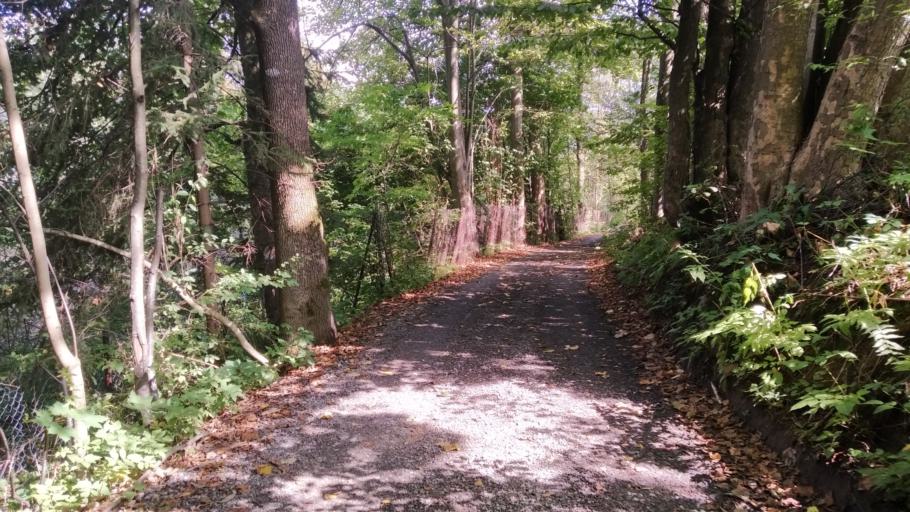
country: PL
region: Lesser Poland Voivodeship
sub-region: Powiat nowotarski
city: Kroscienko nad Dunajcem
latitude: 49.4395
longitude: 20.4196
